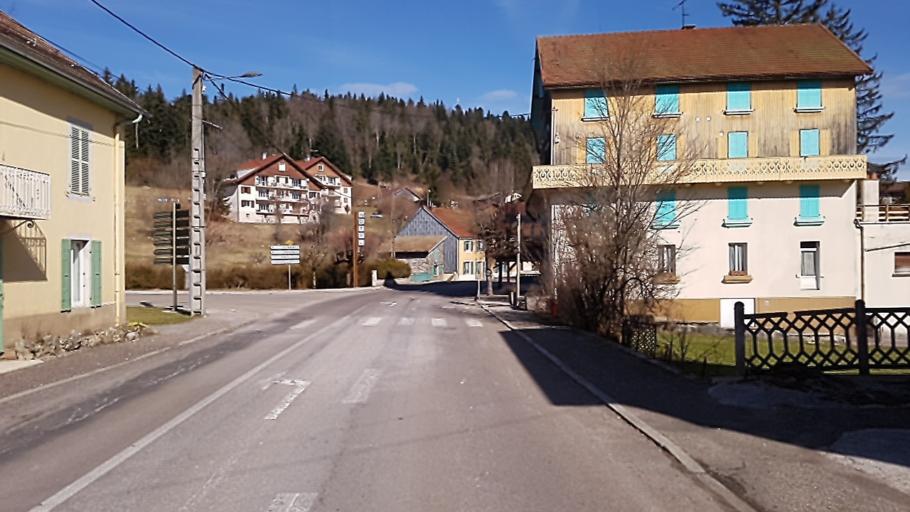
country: FR
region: Franche-Comte
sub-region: Departement du Jura
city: Champagnole
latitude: 46.6540
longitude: 5.9411
